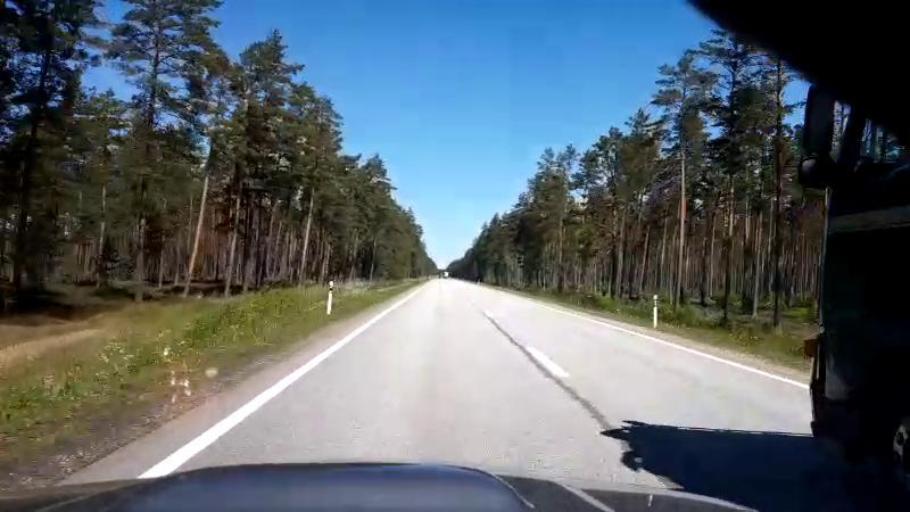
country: LV
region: Salacgrivas
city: Salacgriva
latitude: 57.5514
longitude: 24.4330
